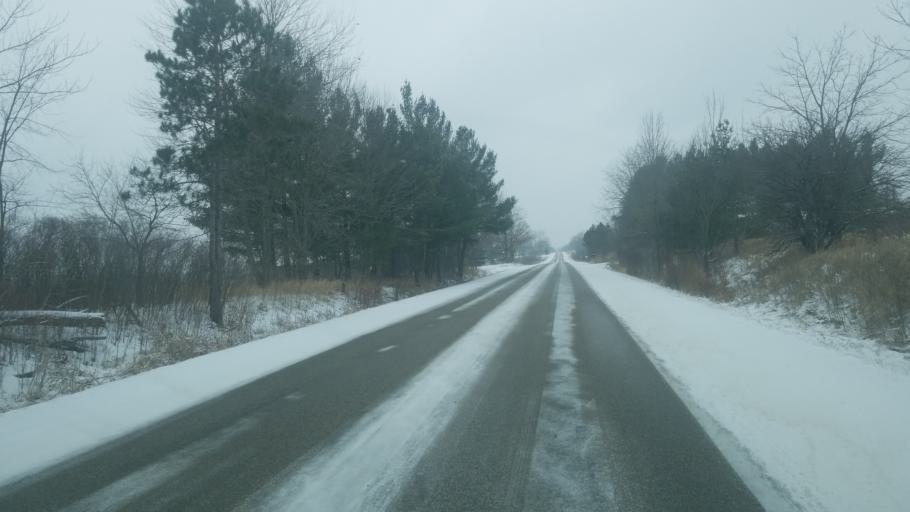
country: US
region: Michigan
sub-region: Osceola County
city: Evart
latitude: 44.1025
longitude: -85.1766
